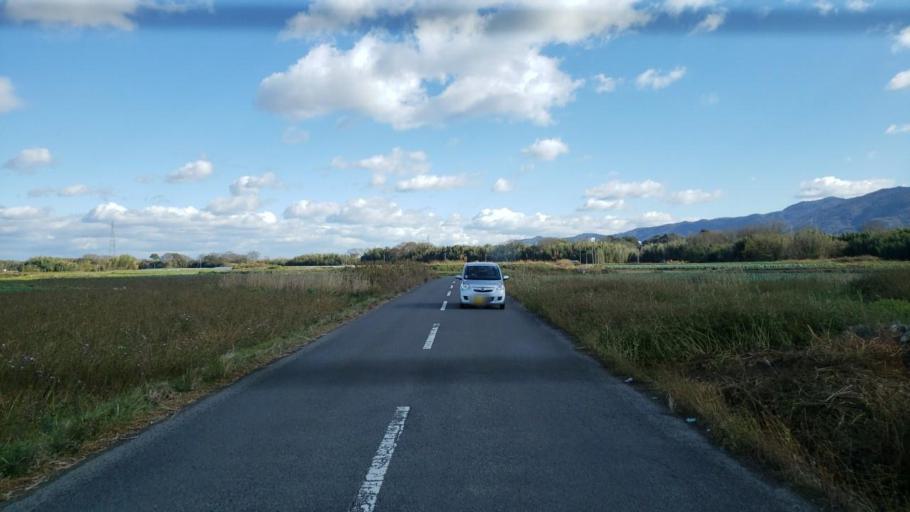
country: JP
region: Tokushima
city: Kamojimacho-jogejima
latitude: 34.0699
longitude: 134.3093
